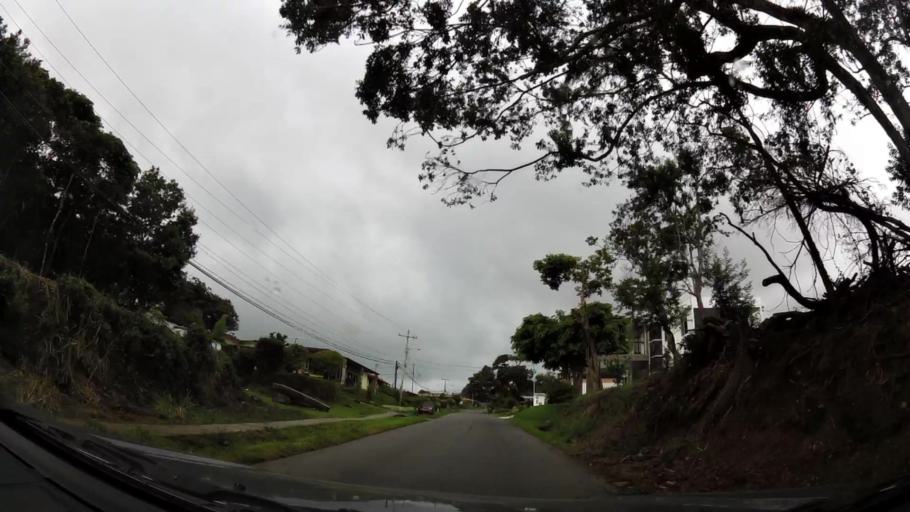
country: PA
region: Chiriqui
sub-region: Distrito Boquete
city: Boquete
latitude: 8.7569
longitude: -82.4347
